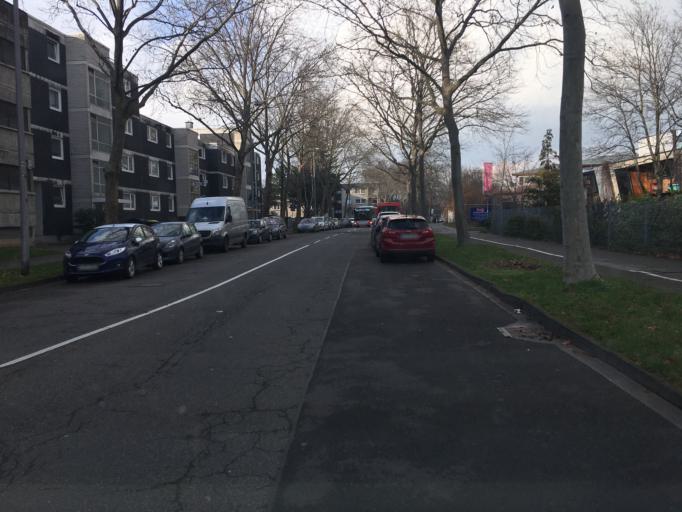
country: DE
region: North Rhine-Westphalia
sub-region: Regierungsbezirk Koln
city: Mengenich
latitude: 51.0285
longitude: 6.8951
